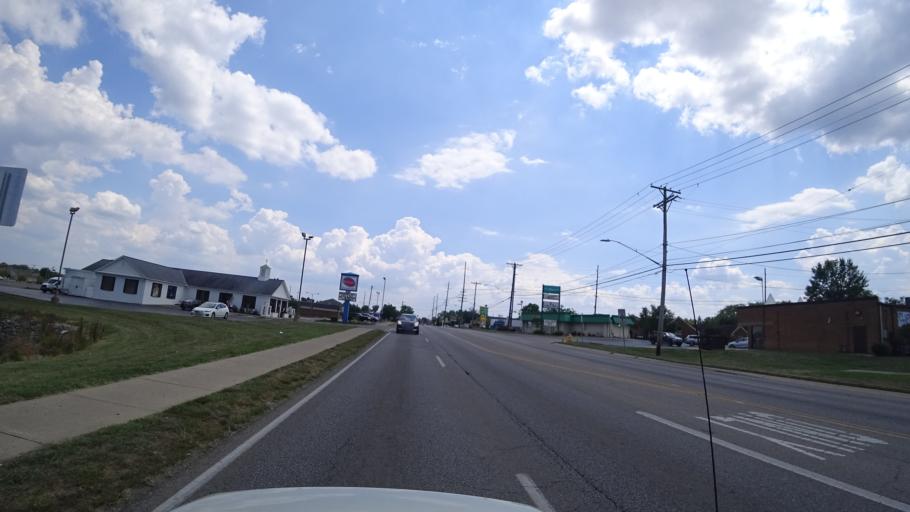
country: US
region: Ohio
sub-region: Butler County
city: Hamilton
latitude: 39.4216
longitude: -84.5913
